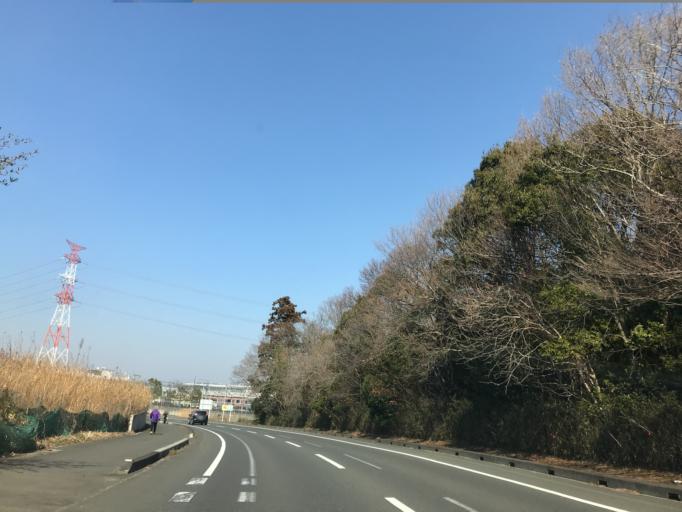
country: JP
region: Ibaraki
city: Moriya
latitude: 35.9614
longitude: 139.9964
